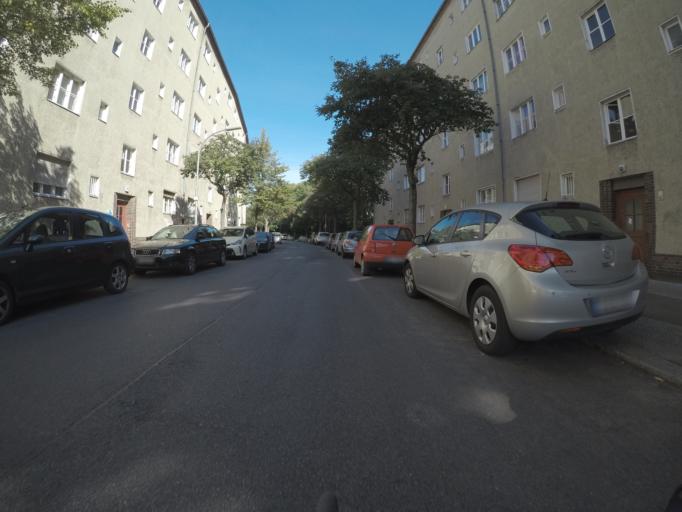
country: DE
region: Berlin
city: Gesundbrunnen
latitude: 52.5589
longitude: 13.3964
